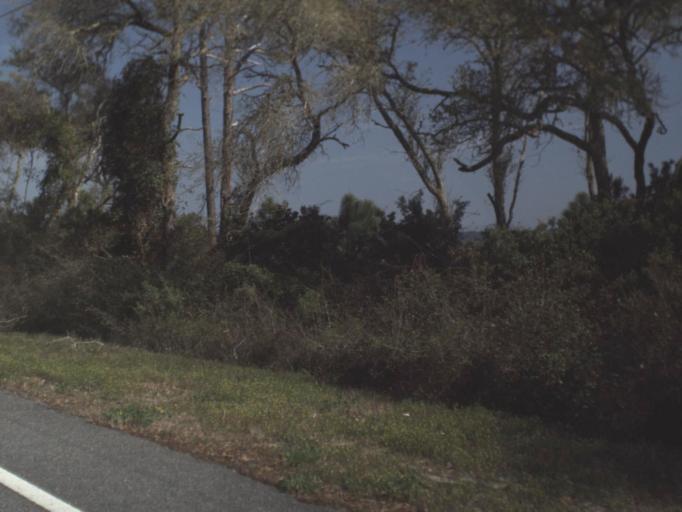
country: US
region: Florida
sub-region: Franklin County
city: Eastpoint
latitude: 29.7684
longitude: -84.8031
